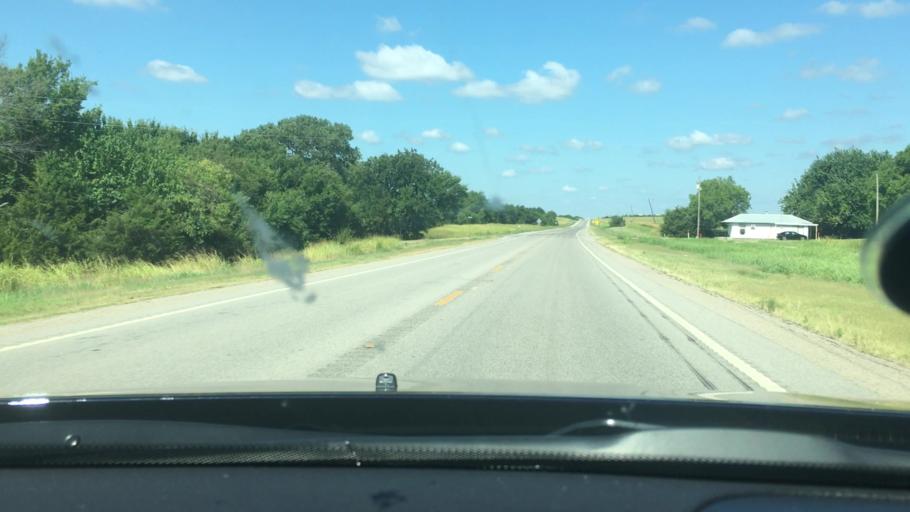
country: US
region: Oklahoma
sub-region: Marshall County
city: Oakland
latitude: 34.0999
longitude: -96.8443
